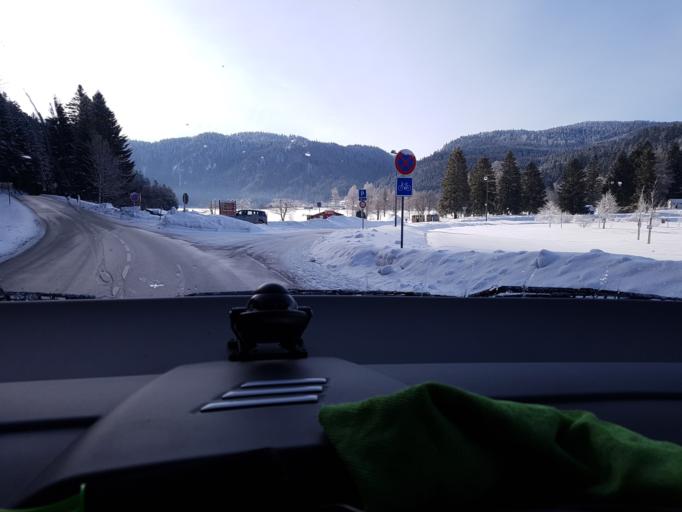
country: FR
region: Lorraine
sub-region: Departement des Vosges
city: Xonrupt-Longemer
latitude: 48.0807
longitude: 6.9478
